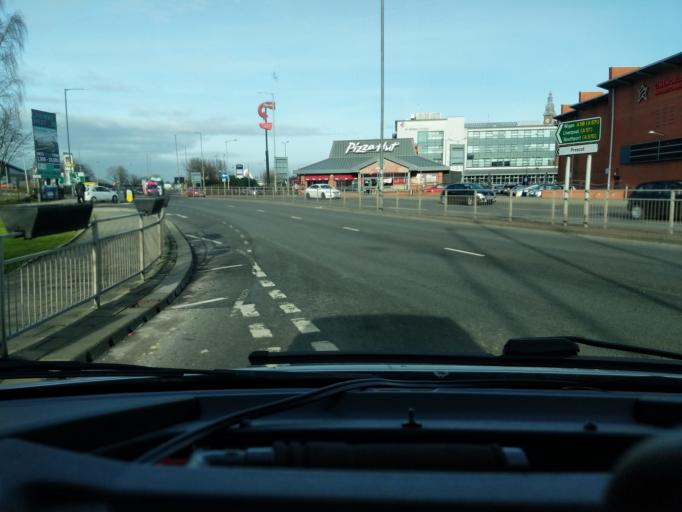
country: GB
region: England
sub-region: St. Helens
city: St Helens
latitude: 53.4510
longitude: -2.7410
